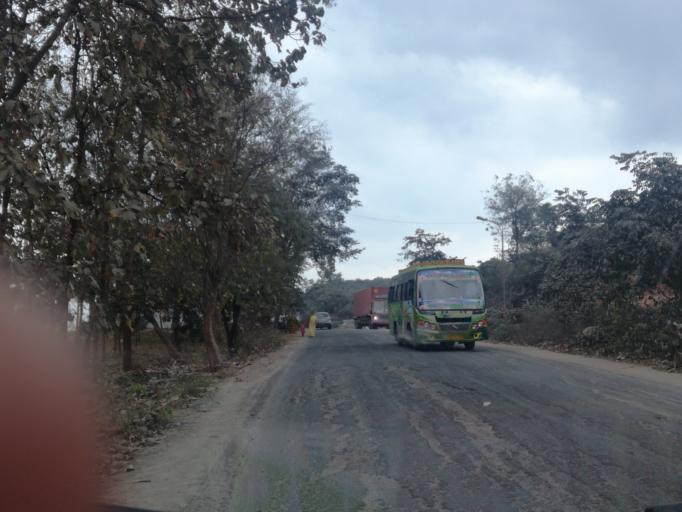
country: IN
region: Andhra Pradesh
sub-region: Chittoor
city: Ramapuram
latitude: 13.0906
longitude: 79.1340
